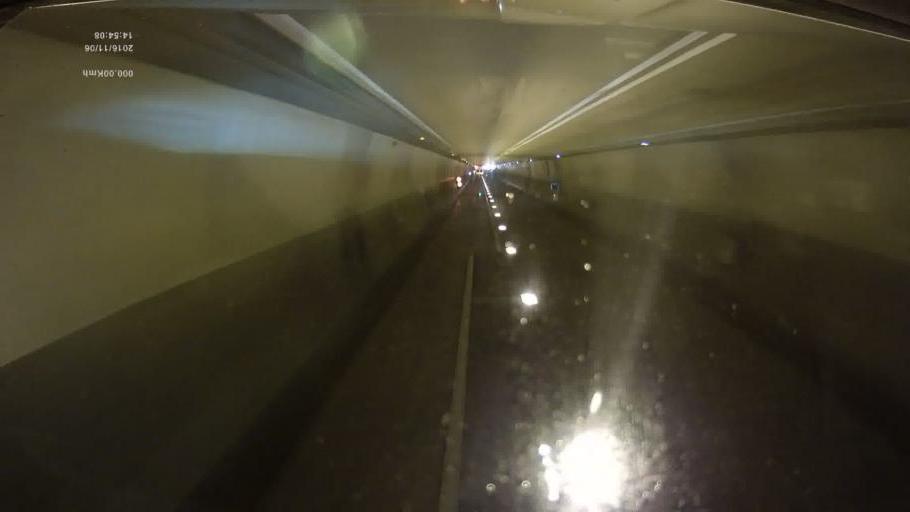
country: SK
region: Kosicky
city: Krompachy
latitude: 49.0046
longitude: 20.8709
